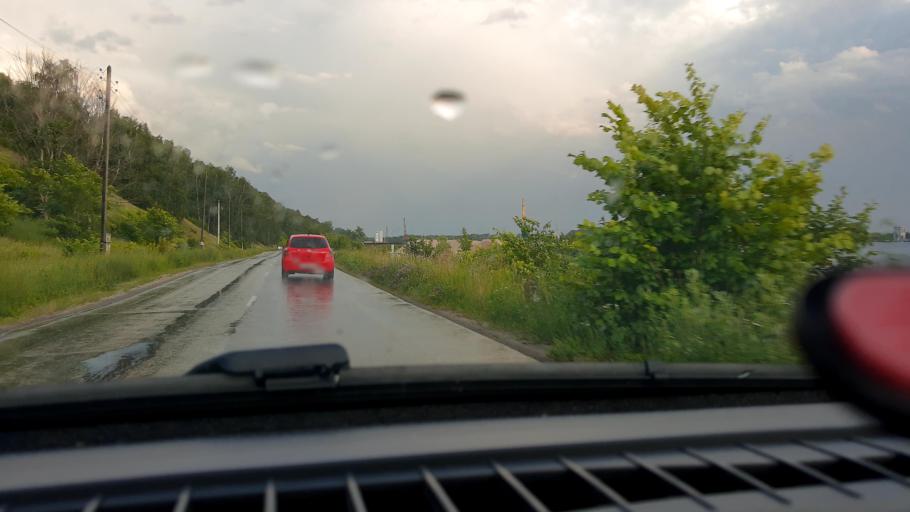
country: RU
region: Nizjnij Novgorod
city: Gorodets
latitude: 56.6773
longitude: 43.4412
